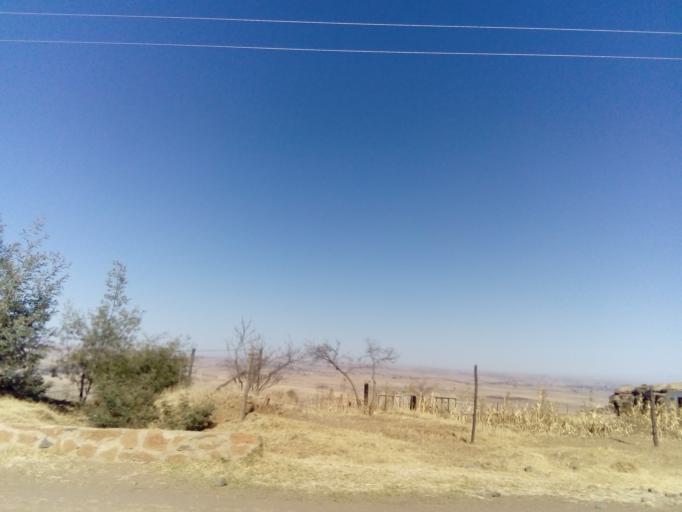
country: LS
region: Berea
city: Teyateyaneng
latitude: -29.1279
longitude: 27.8355
